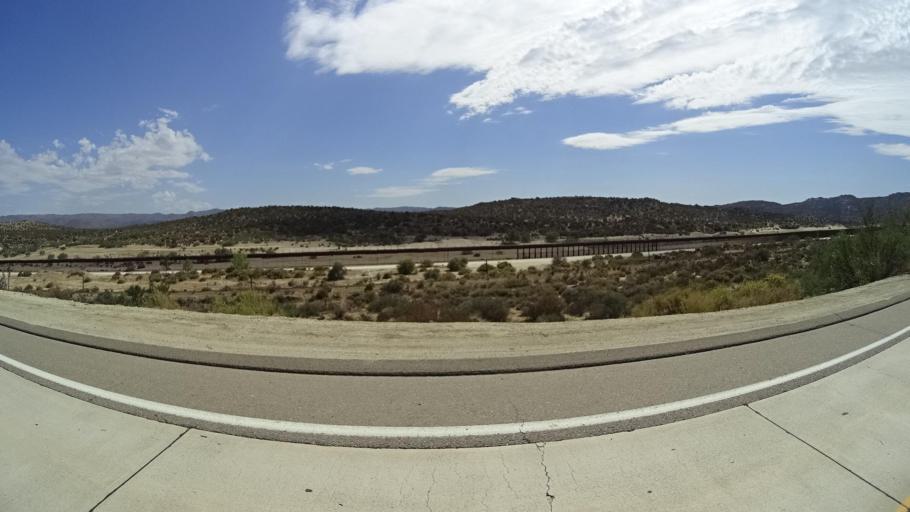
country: MX
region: Baja California
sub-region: Tecate
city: Cereso del Hongo
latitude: 32.6124
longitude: -116.2026
